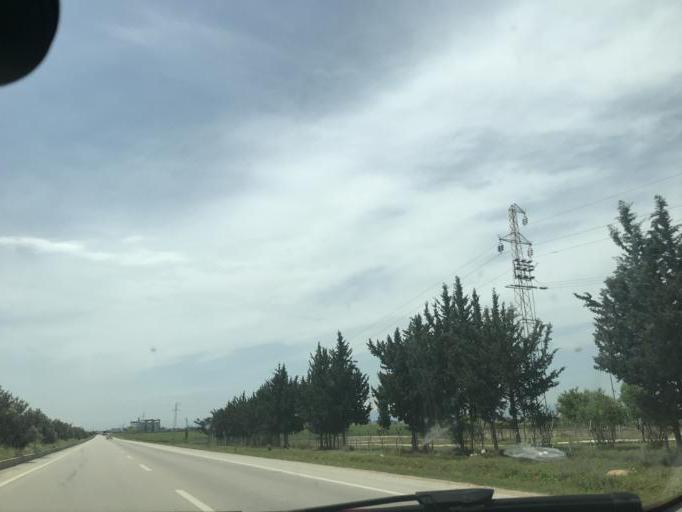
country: TR
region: Adana
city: Yuregir
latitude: 36.9759
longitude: 35.4853
